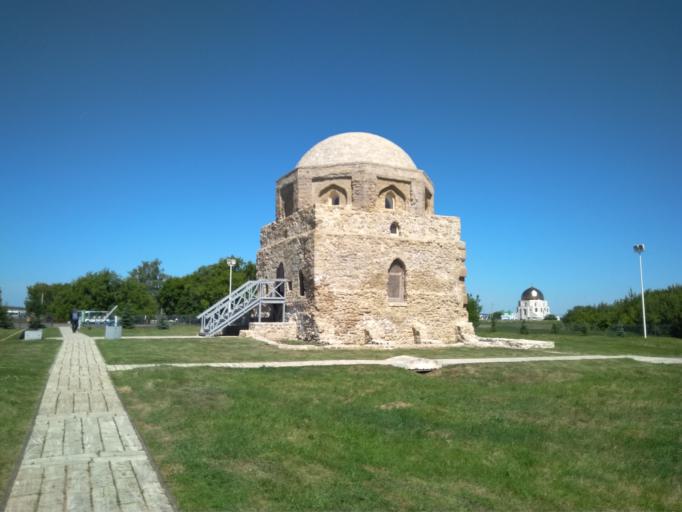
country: RU
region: Tatarstan
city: Bolgar
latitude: 54.9818
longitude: 49.0544
